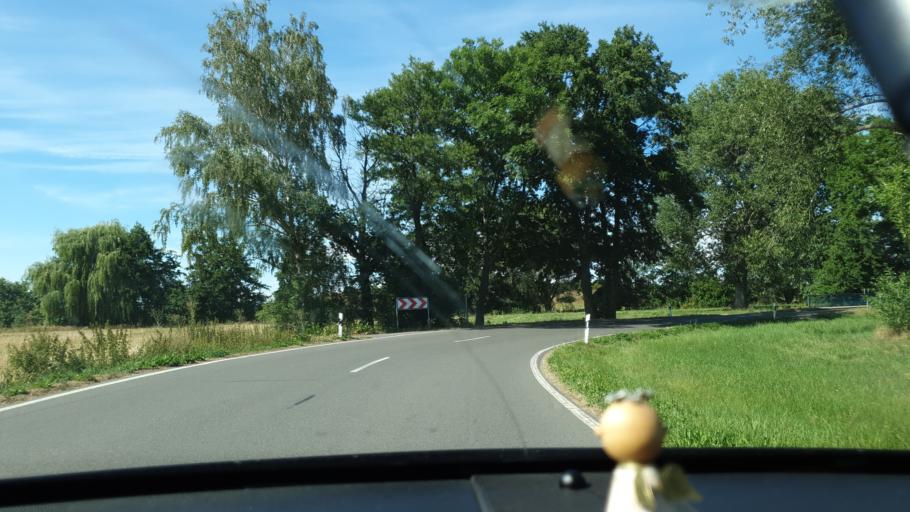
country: DE
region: Saxony
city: Mockrehna
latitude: 51.4863
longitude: 12.8227
